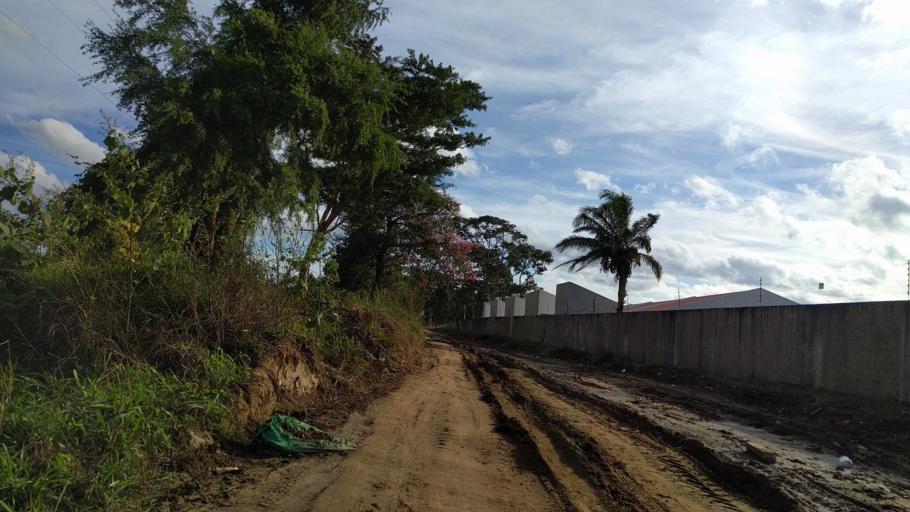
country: BO
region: Santa Cruz
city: Santa Cruz de la Sierra
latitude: -17.8514
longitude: -63.2587
